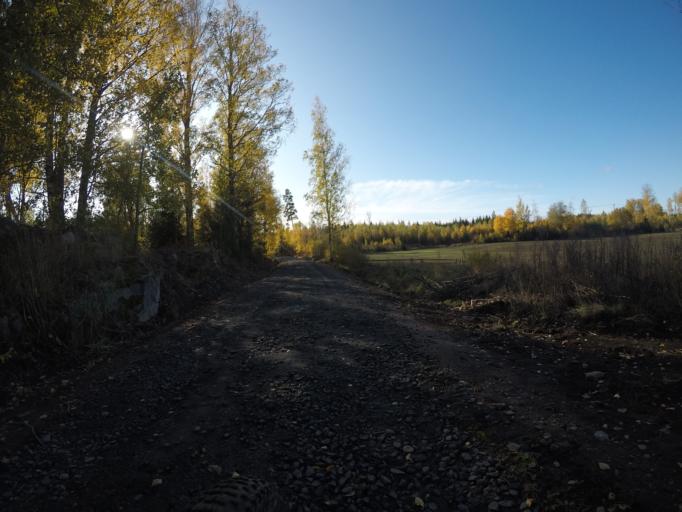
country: SE
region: Vaestmanland
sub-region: Kungsors Kommun
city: Kungsoer
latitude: 59.3152
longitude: 16.0987
